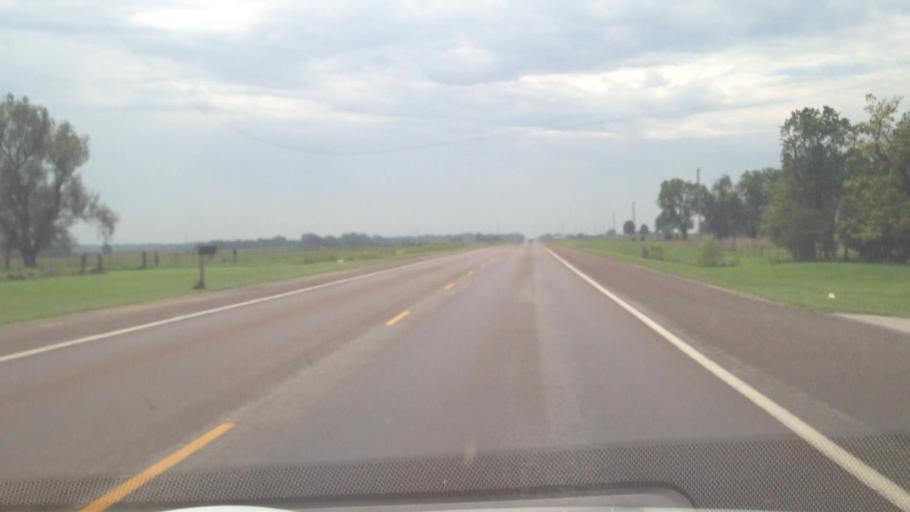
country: US
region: Kansas
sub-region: Crawford County
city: Girard
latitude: 37.4644
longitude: -94.8331
